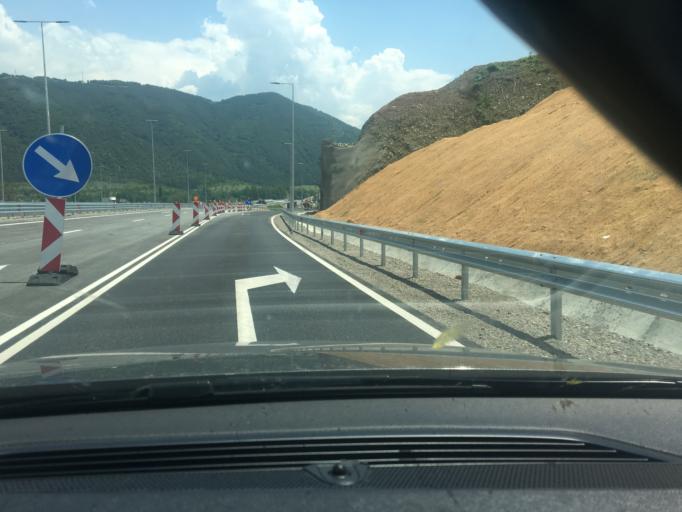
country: BG
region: Blagoevgrad
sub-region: Obshtina Blagoevgrad
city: Blagoevgrad
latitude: 41.9657
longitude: 23.0938
